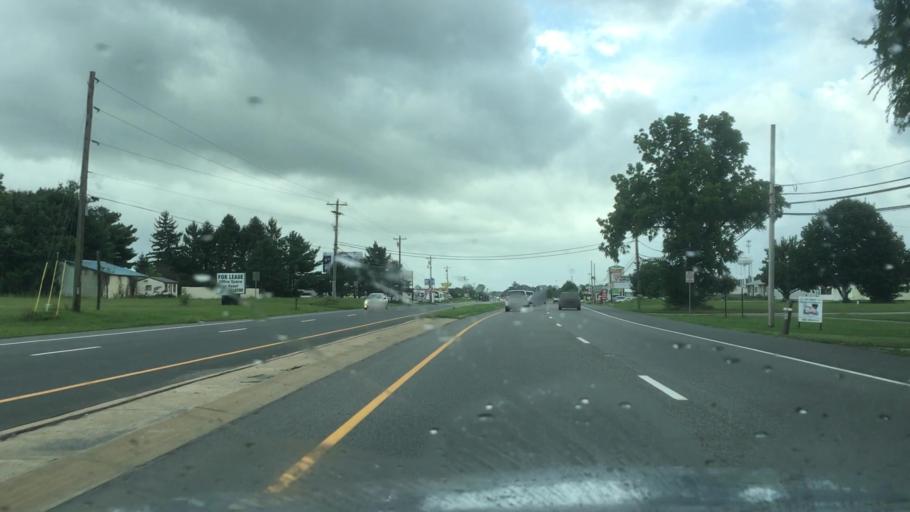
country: US
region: Delaware
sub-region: Kent County
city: Smyrna
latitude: 39.2879
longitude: -75.5952
